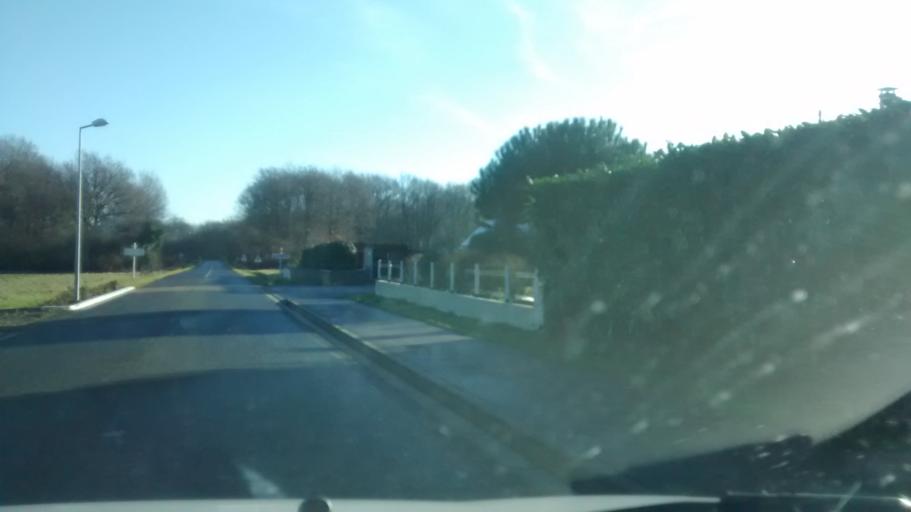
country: FR
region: Centre
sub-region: Departement d'Indre-et-Loire
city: Monnaie
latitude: 47.4960
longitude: 0.8026
